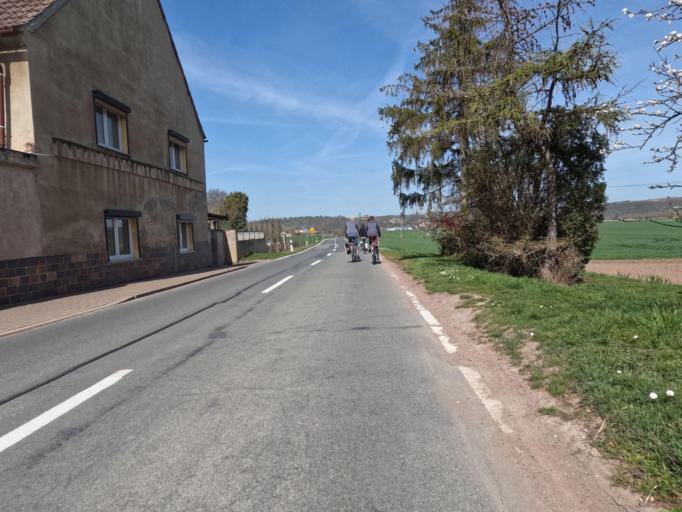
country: DE
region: Saxony-Anhalt
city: Beesenstedt
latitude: 51.6026
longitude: 11.7495
